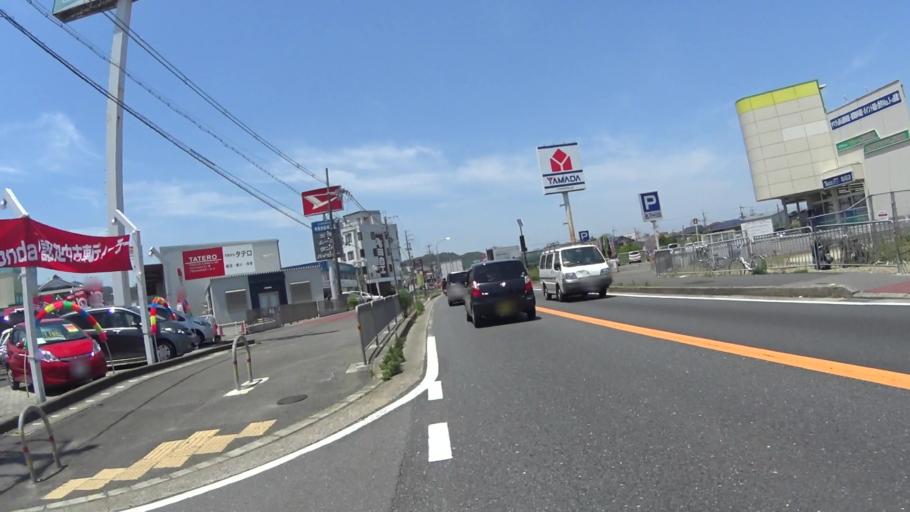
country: JP
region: Kyoto
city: Kameoka
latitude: 35.0046
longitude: 135.5870
